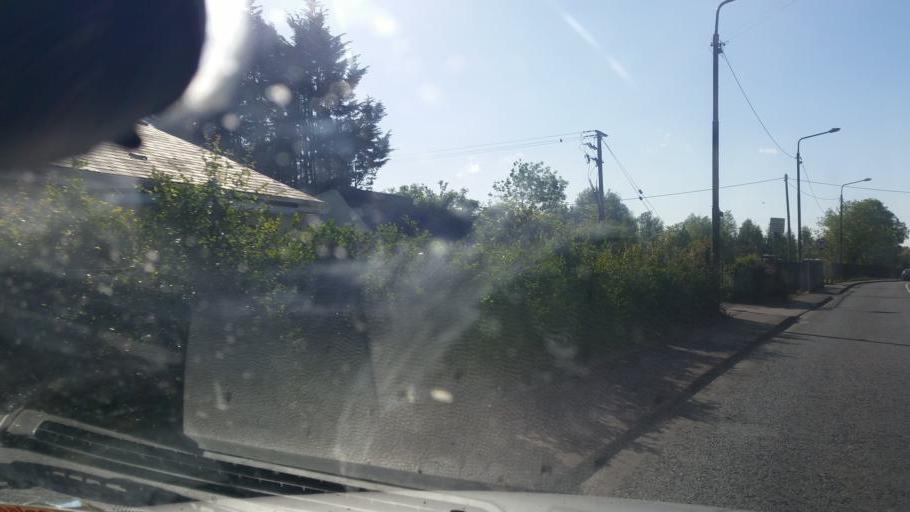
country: IE
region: Leinster
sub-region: Fingal County
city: Blanchardstown
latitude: 53.4012
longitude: -6.3945
